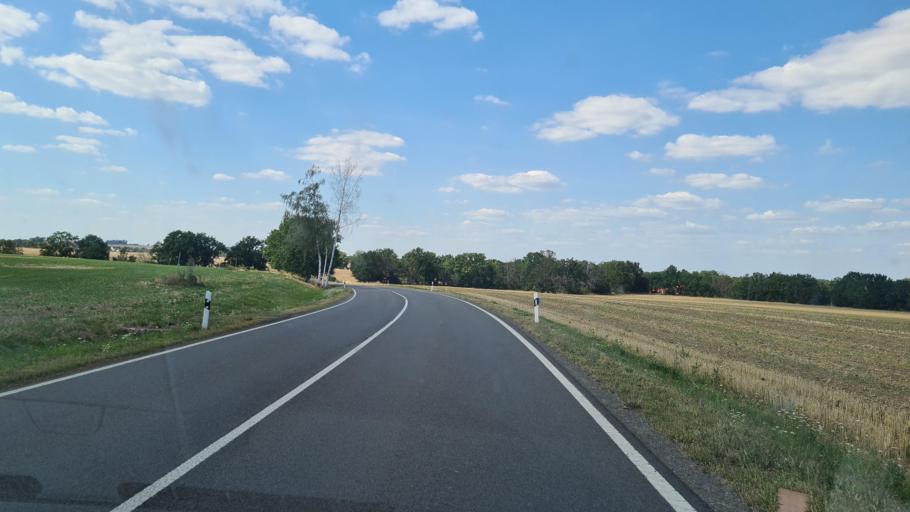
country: DE
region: Saxony
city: Machern
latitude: 51.4079
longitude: 12.6419
